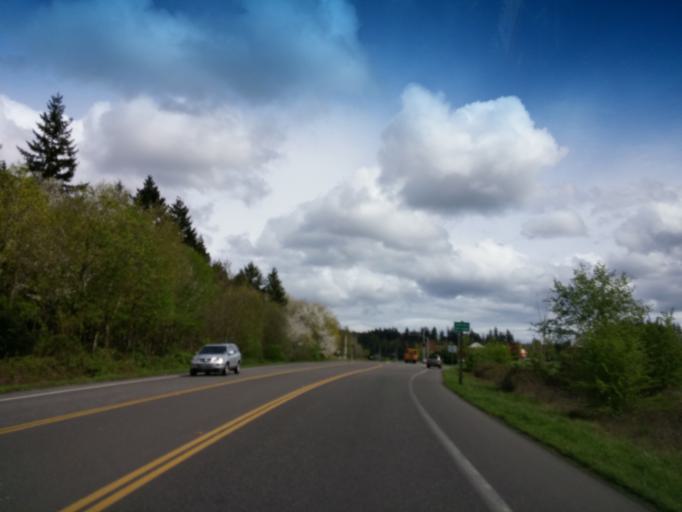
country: US
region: Oregon
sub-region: Washington County
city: Cedar Hills
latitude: 45.5170
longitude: -122.7951
